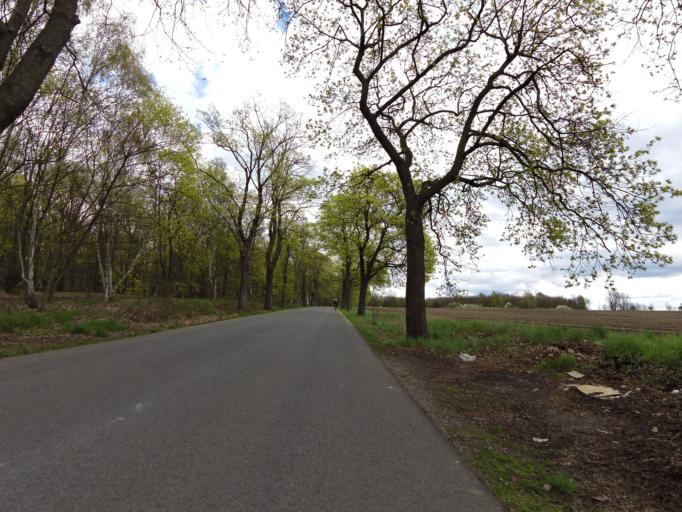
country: DE
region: Berlin
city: Lichtenrade
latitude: 52.3738
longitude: 13.4262
